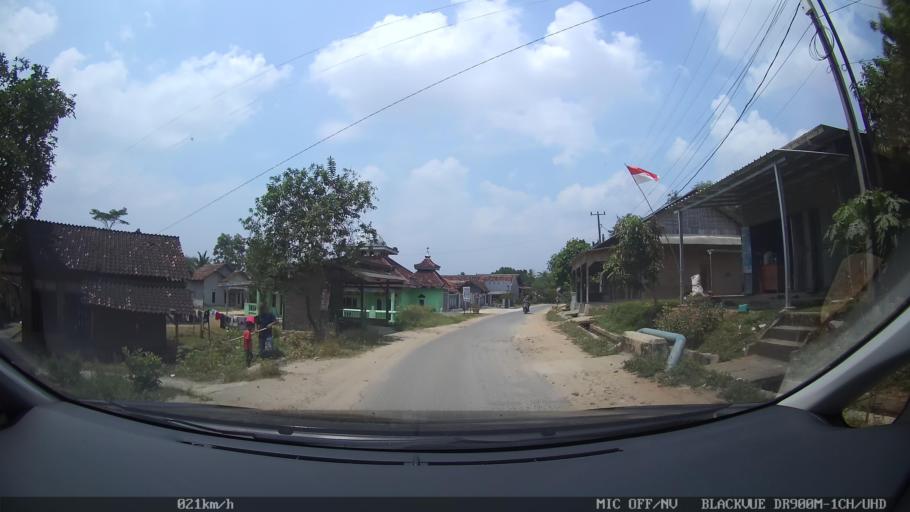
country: ID
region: Lampung
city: Pringsewu
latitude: -5.3427
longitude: 104.9871
